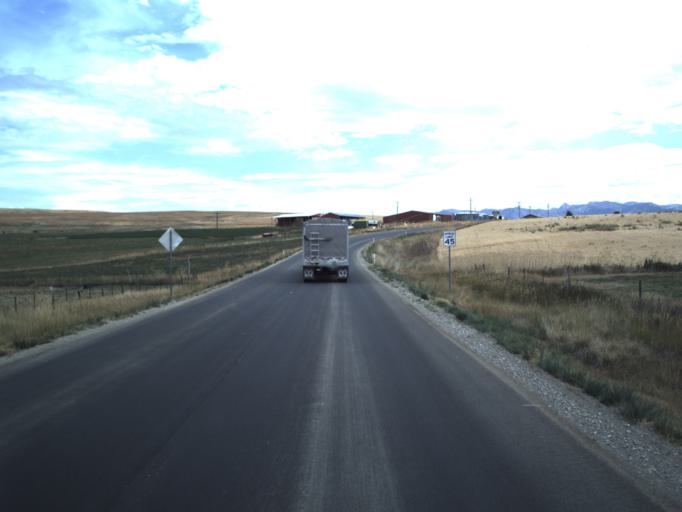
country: US
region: Utah
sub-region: Cache County
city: Benson
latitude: 41.8615
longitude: -111.9767
